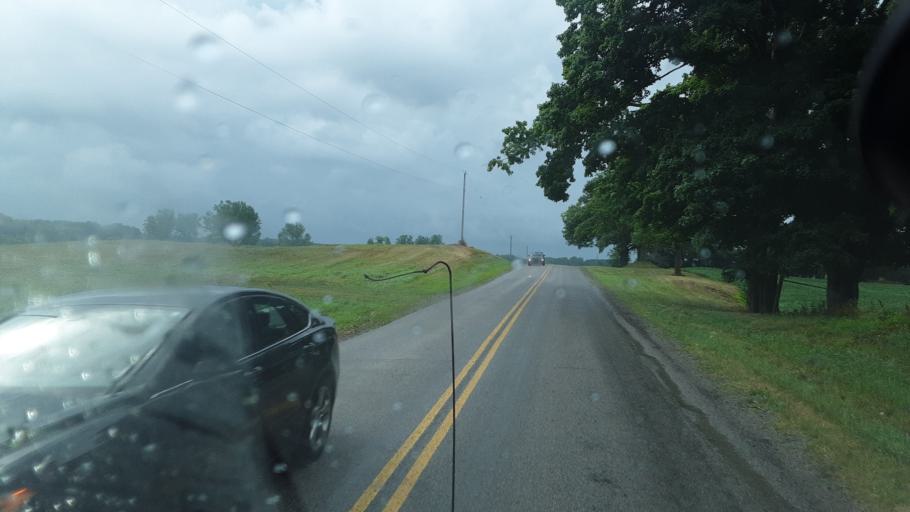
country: US
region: Indiana
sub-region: Steuben County
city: Fremont
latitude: 41.6513
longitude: -84.7926
